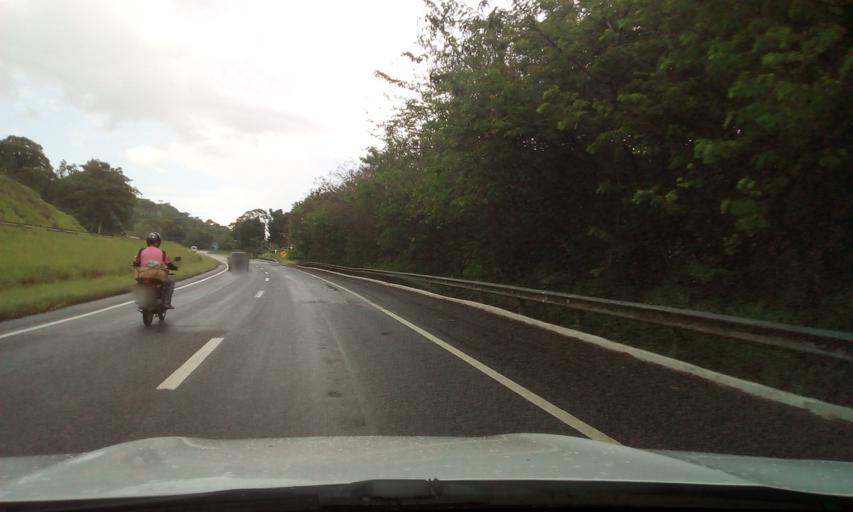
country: BR
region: Pernambuco
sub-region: Cabo De Santo Agostinho
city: Cabo
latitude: -8.3083
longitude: -35.0796
